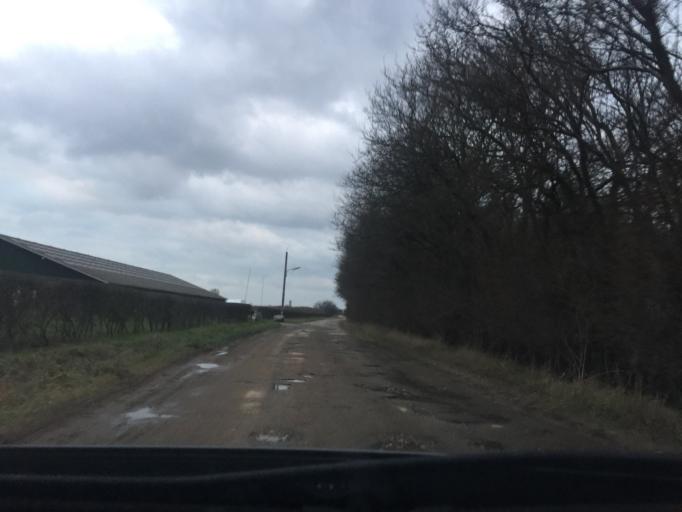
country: DK
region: Capital Region
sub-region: Dragor Kommune
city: Dragor
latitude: 55.5956
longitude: 12.6258
